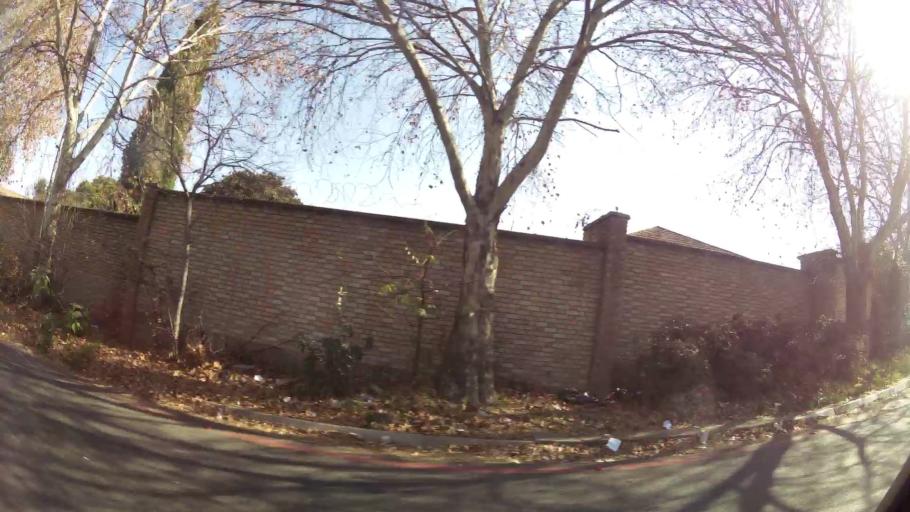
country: ZA
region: Gauteng
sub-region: City of Johannesburg Metropolitan Municipality
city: Johannesburg
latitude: -26.2600
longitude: 28.0578
